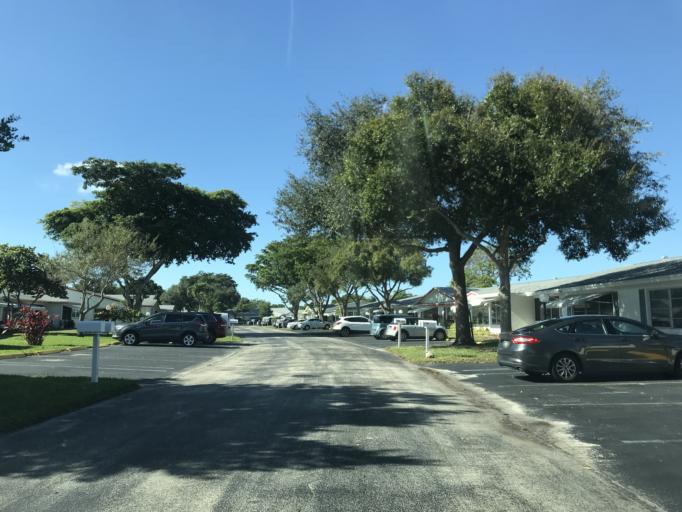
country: US
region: Florida
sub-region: Broward County
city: Plantation
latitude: 26.1394
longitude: -80.2637
